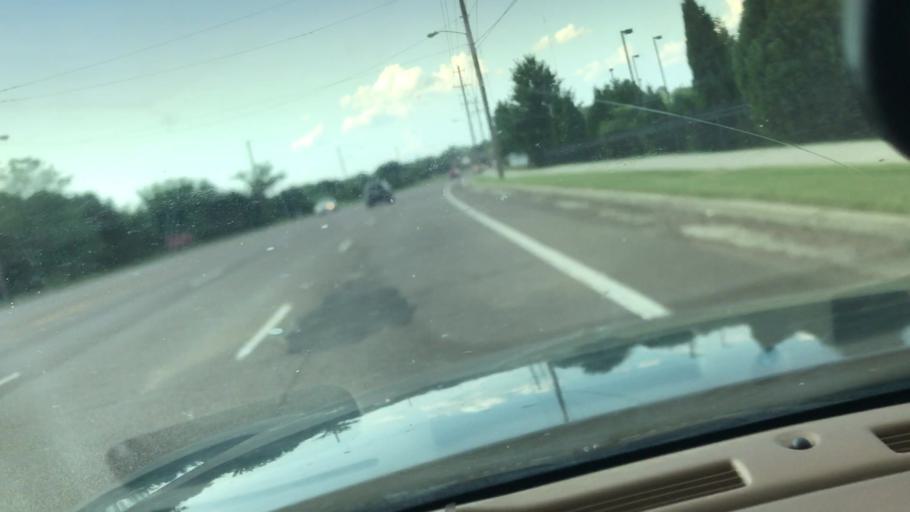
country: US
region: Tennessee
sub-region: Shelby County
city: Bartlett
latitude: 35.1907
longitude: -89.8146
